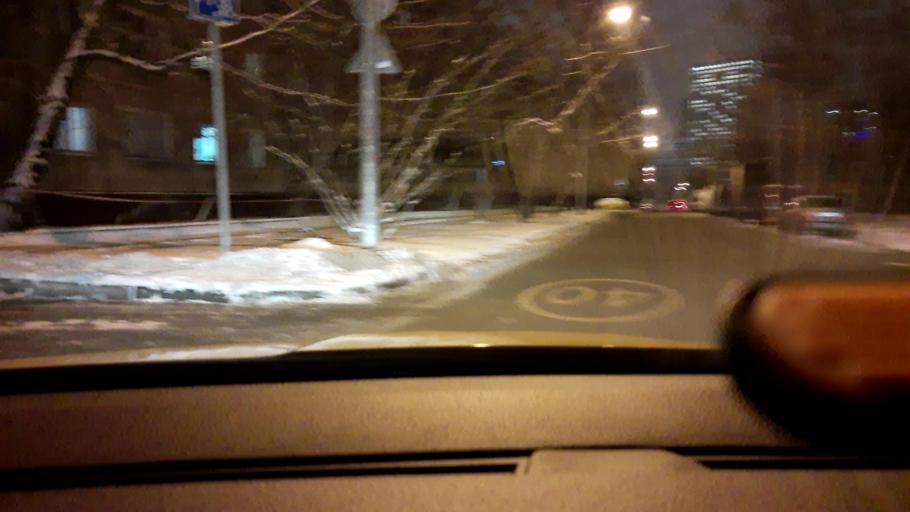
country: RU
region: Moscow
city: Vagonoremont
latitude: 55.8946
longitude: 37.5296
